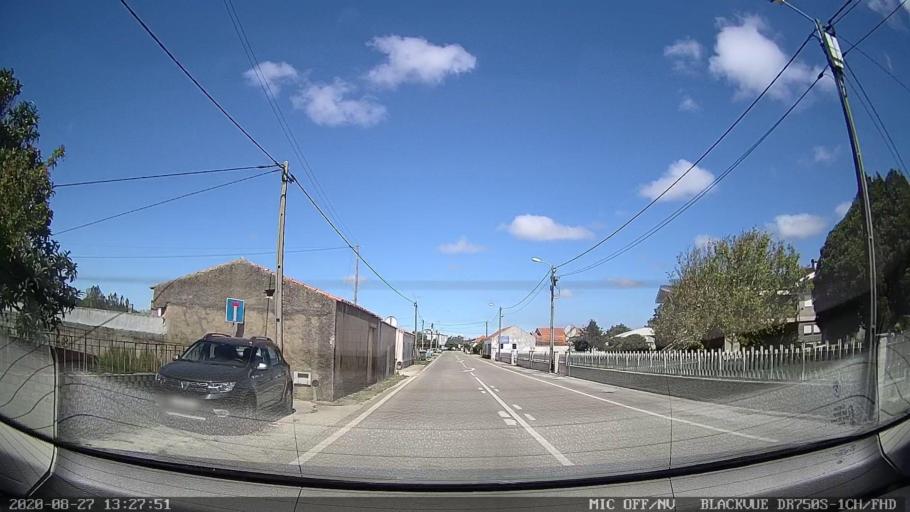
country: PT
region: Aveiro
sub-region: Vagos
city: Vagos
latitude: 40.5264
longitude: -8.6792
